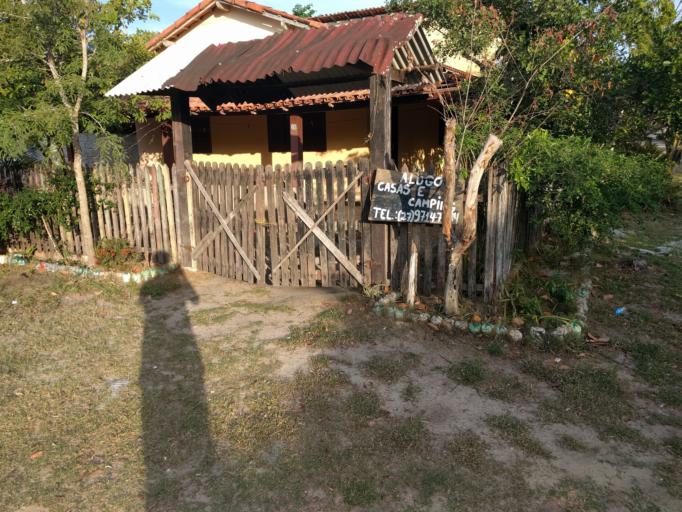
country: BR
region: Espirito Santo
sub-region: Conceicao Da Barra
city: Conceicao da Barra
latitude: -18.4208
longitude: -39.7082
